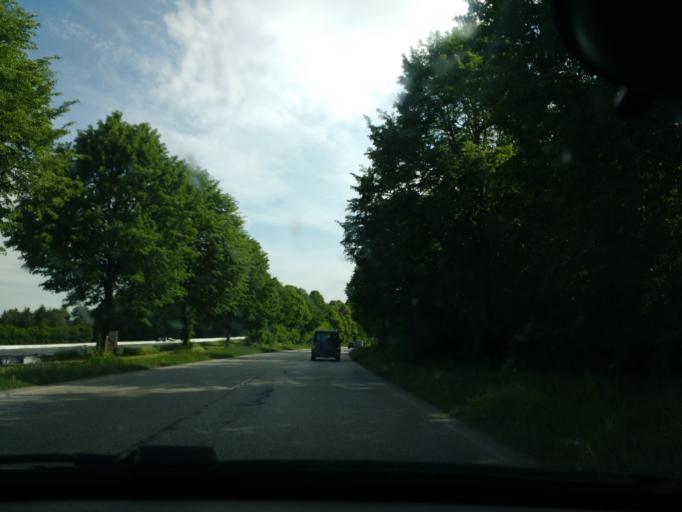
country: DE
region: Schleswig-Holstein
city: Buchholz
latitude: 53.7289
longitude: 10.7382
